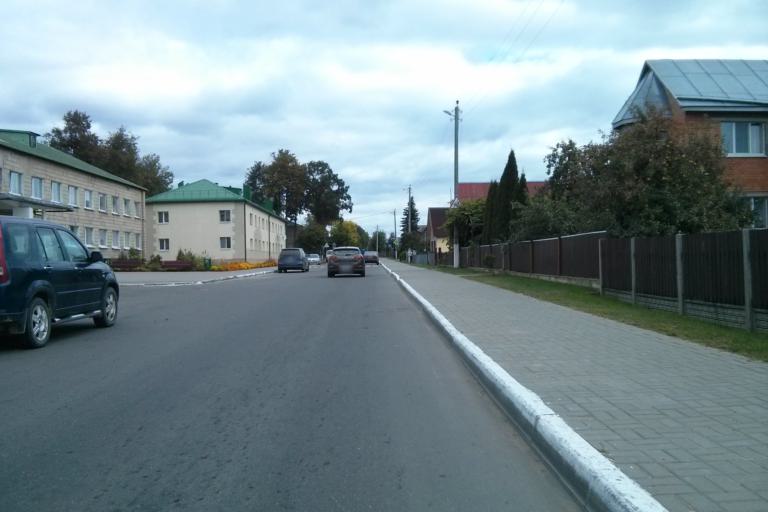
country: BY
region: Minsk
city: Chervyen'
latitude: 53.7129
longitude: 28.4165
